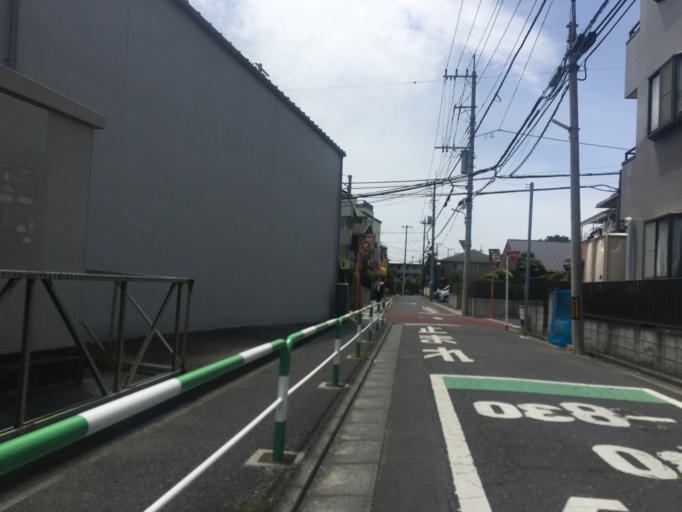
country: JP
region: Saitama
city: Yono
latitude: 35.8451
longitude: 139.6399
